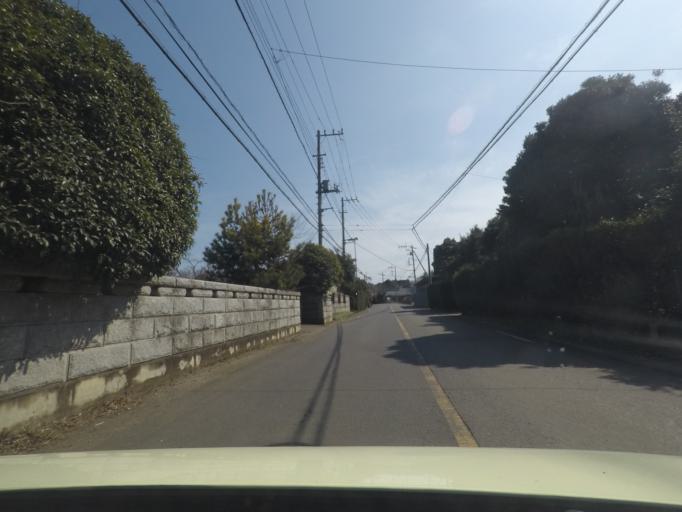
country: JP
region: Ibaraki
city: Okunoya
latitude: 36.2047
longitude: 140.4288
